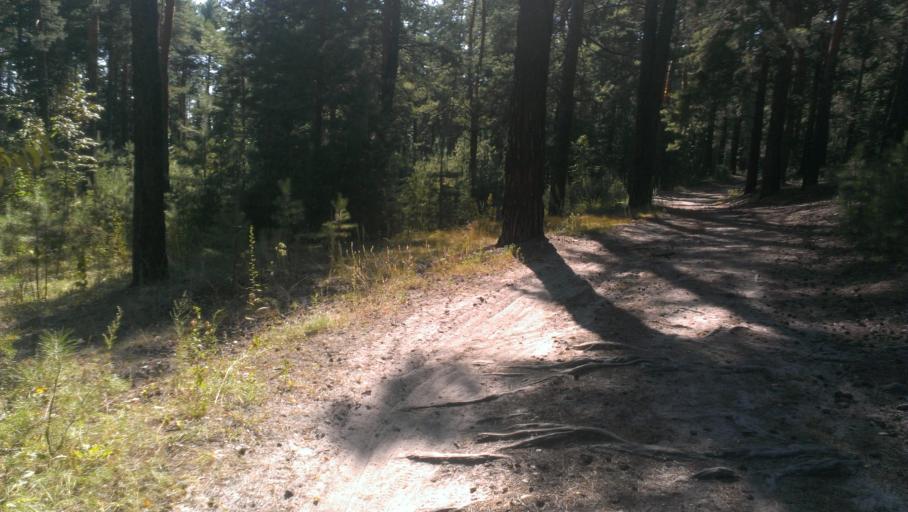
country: RU
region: Altai Krai
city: Yuzhnyy
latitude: 53.3150
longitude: 83.6874
